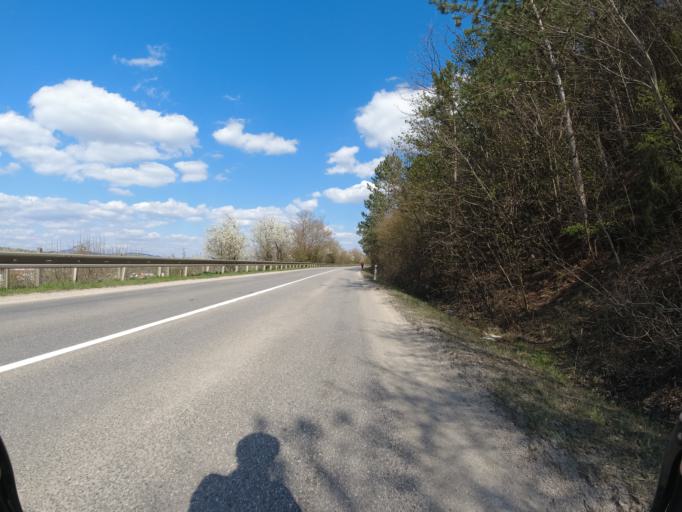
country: SK
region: Trenciansky
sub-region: Okres Nove Mesto nad Vahom
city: Nove Mesto nad Vahom
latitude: 48.7854
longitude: 17.7696
